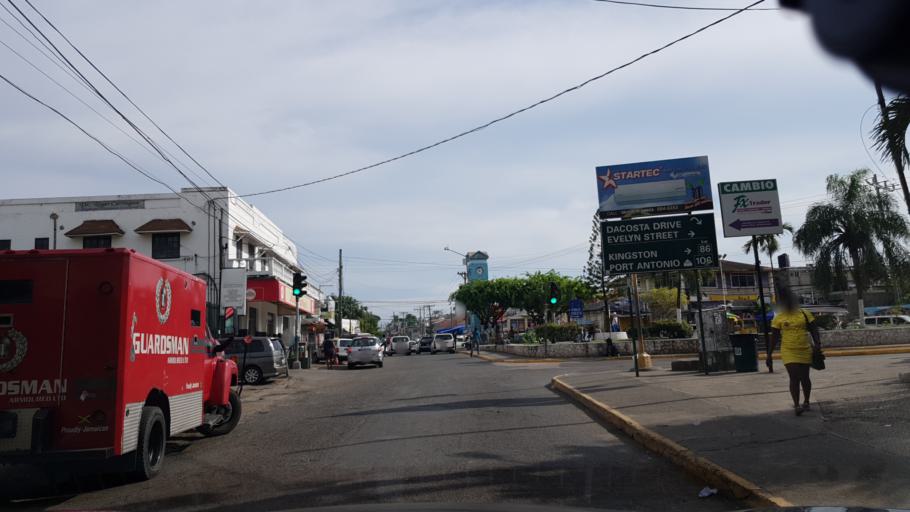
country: JM
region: Saint Ann
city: Ocho Rios
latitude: 18.4101
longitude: -77.1034
